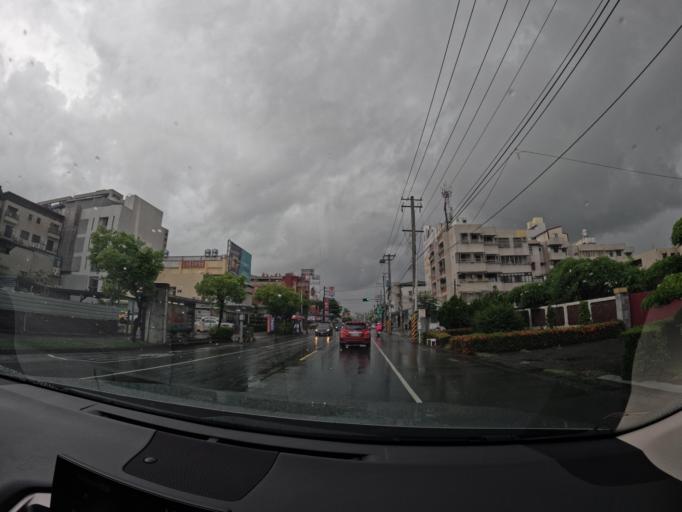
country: TW
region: Taiwan
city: Fengshan
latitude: 22.6519
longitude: 120.3408
